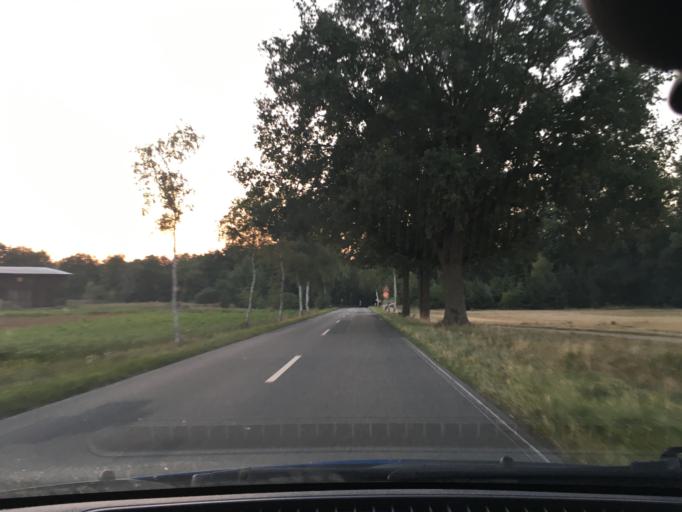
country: DE
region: Lower Saxony
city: Embsen
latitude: 53.1553
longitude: 10.3488
